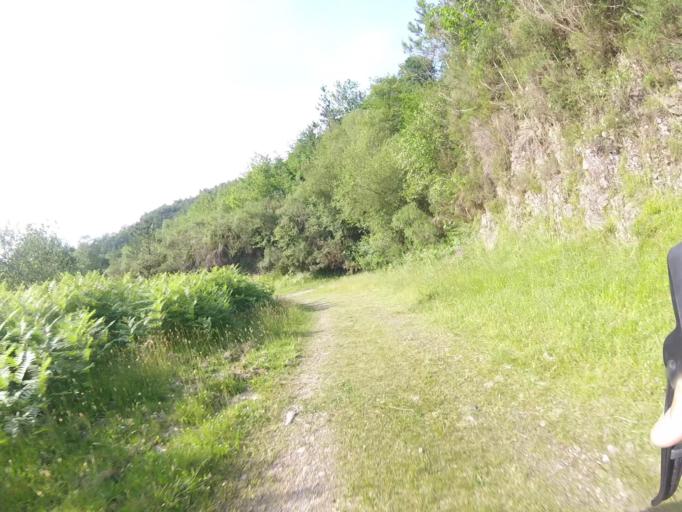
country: ES
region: Navarre
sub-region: Provincia de Navarra
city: Arano
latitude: 43.2303
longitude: -1.8659
